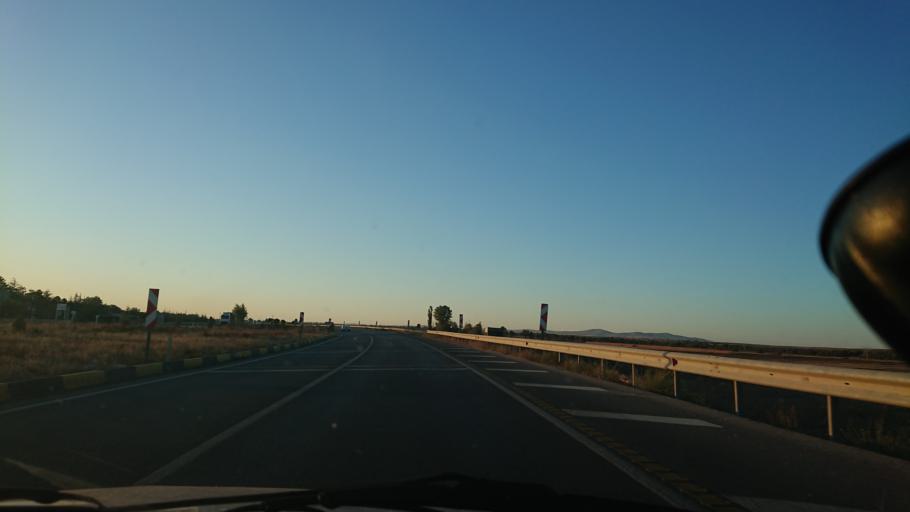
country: TR
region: Eskisehir
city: Mahmudiye
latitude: 39.5377
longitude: 30.9435
